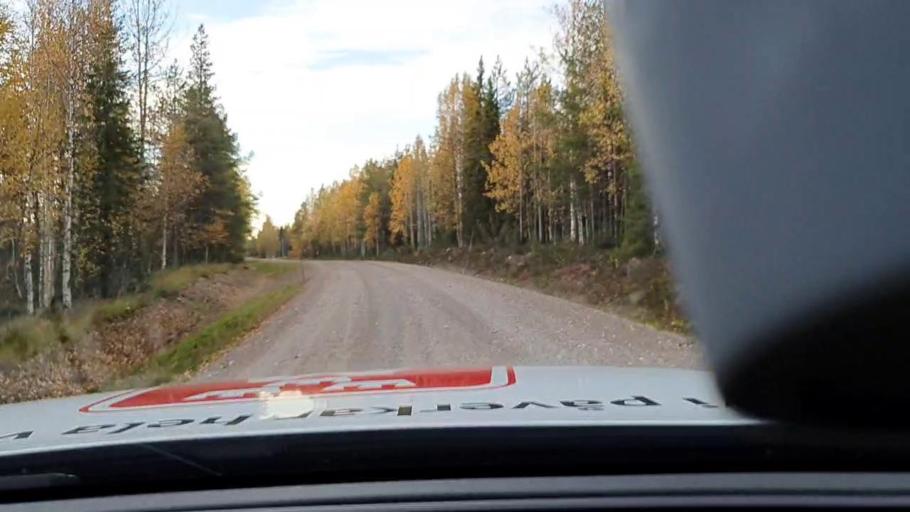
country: SE
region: Norrbotten
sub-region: Lulea Kommun
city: Ranea
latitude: 66.2689
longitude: 22.2600
